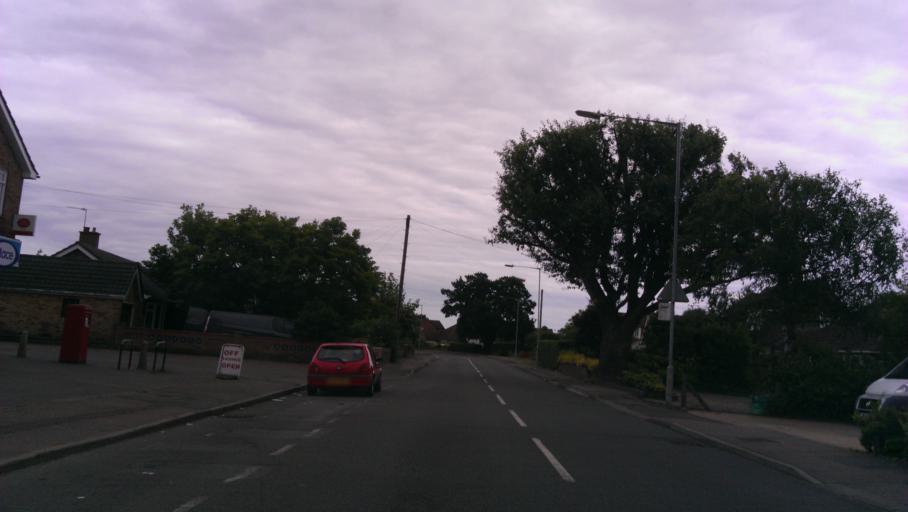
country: GB
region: England
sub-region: Essex
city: Eight Ash Green
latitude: 51.8785
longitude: 0.8385
